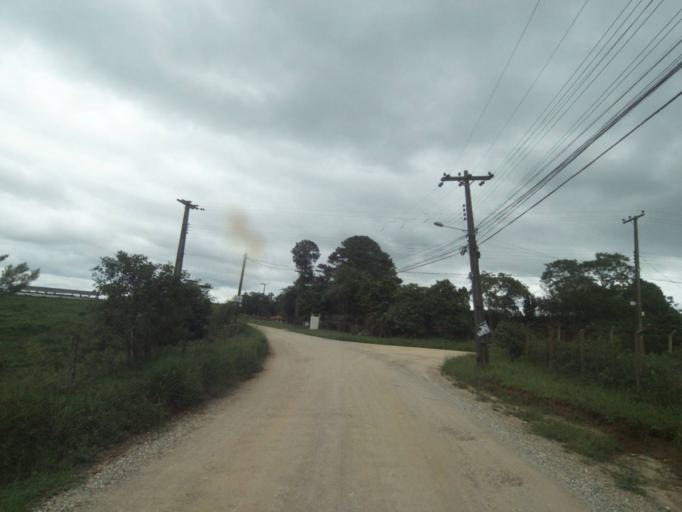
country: BR
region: Parana
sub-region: Campina Grande Do Sul
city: Campina Grande do Sul
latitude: -25.3245
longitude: -49.0875
